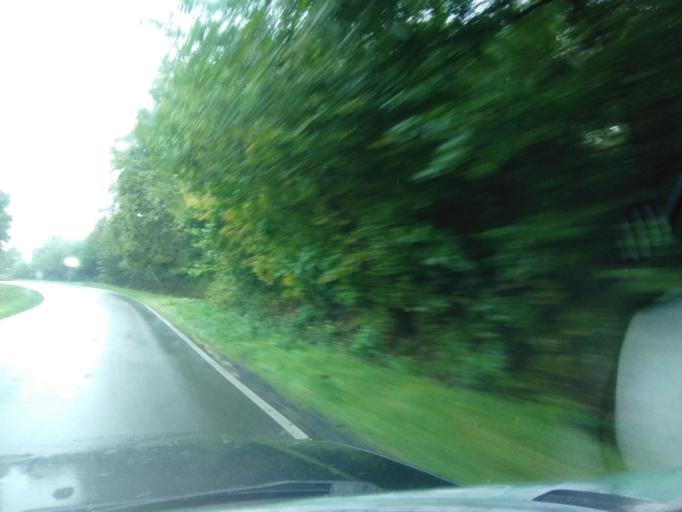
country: PL
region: Subcarpathian Voivodeship
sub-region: Powiat ropczycko-sedziszowski
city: Niedzwiada
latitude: 50.0412
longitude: 21.5442
